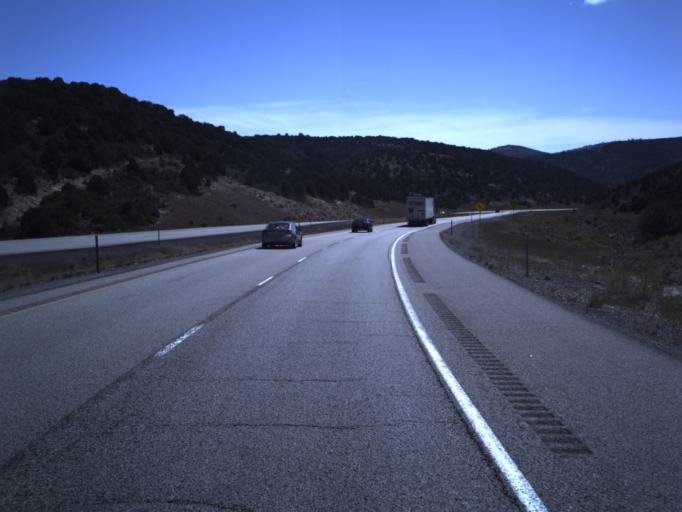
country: US
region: Utah
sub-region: Wayne County
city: Loa
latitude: 38.7774
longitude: -111.4798
